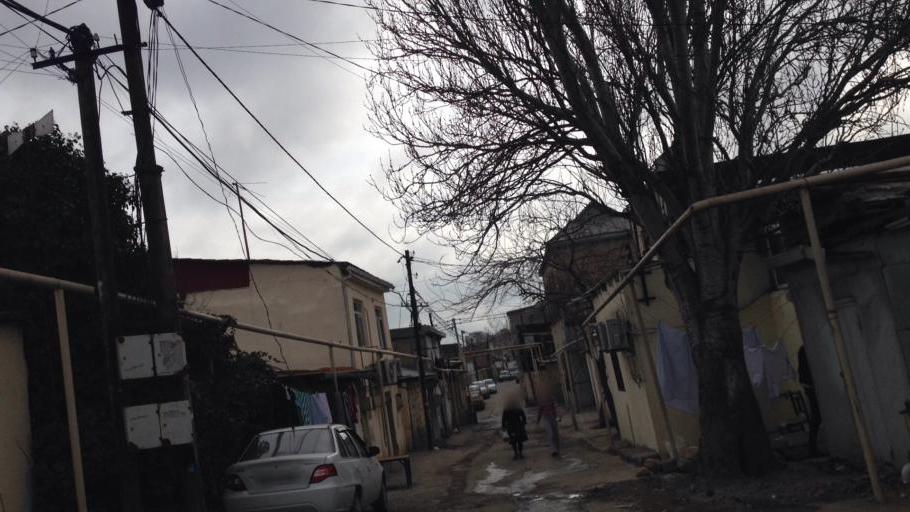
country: AZ
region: Baki
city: Bilajari
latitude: 40.4011
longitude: 49.8275
